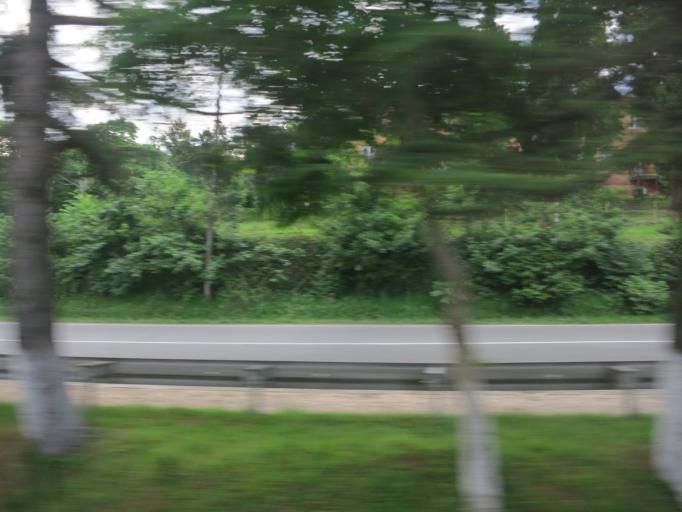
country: GE
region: Ajaria
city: Makhinjauri
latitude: 41.6853
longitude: 41.7015
